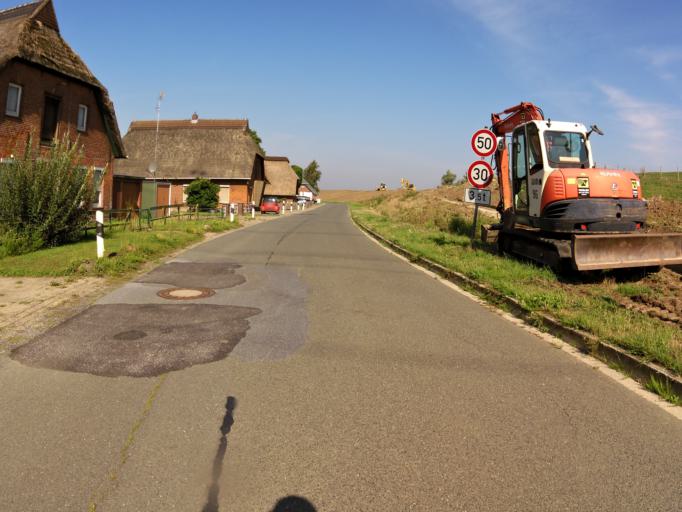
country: DE
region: Lower Saxony
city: Neuenkirchen
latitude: 53.1997
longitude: 8.4976
